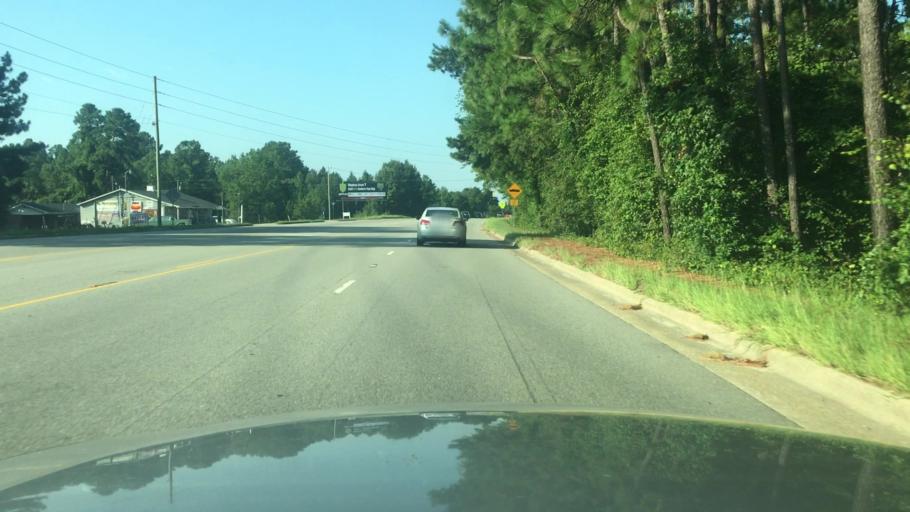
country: US
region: North Carolina
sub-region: Cumberland County
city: Eastover
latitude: 35.1837
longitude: -78.8535
